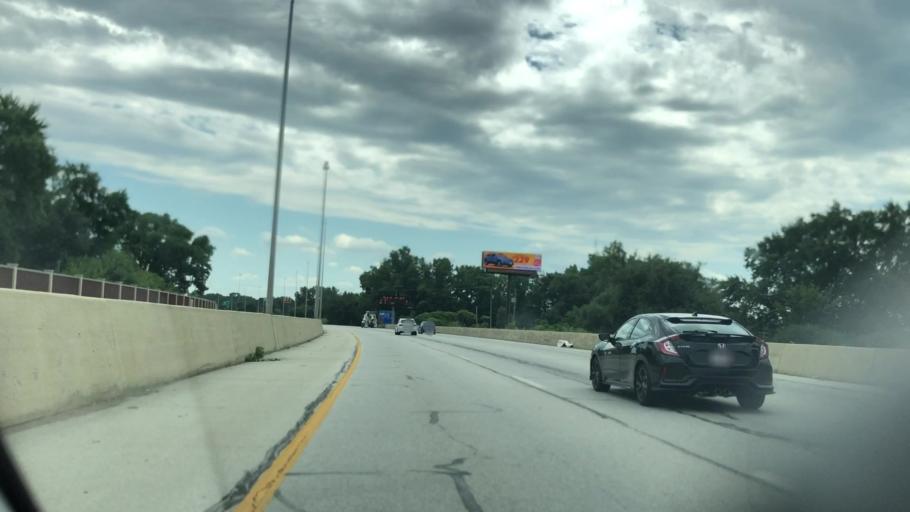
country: US
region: Ohio
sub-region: Summit County
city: Fairlawn
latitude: 41.0903
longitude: -81.5842
